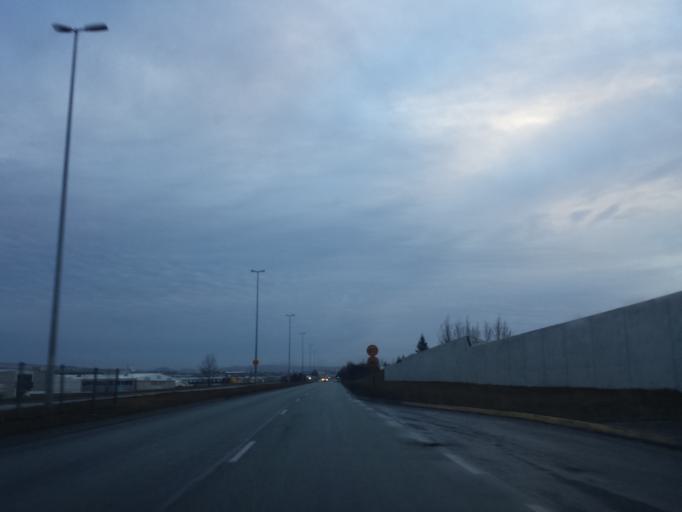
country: IS
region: Capital Region
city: Reykjavik
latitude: 64.1403
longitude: -21.8506
